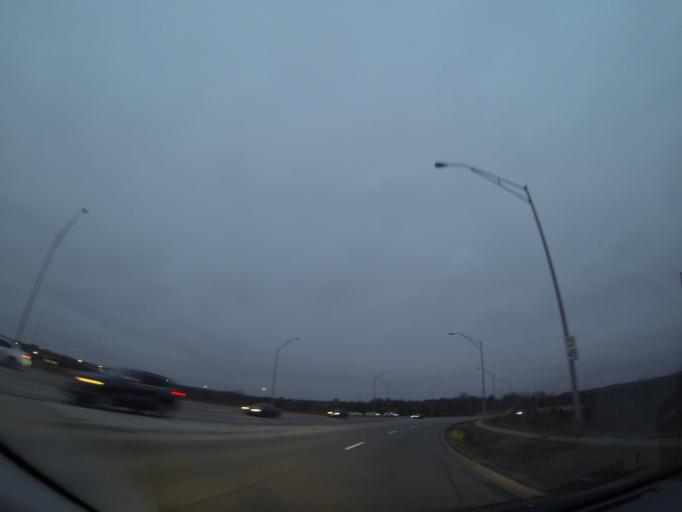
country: US
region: Nebraska
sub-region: Douglas County
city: Elkhorn
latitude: 41.2637
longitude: -96.1791
